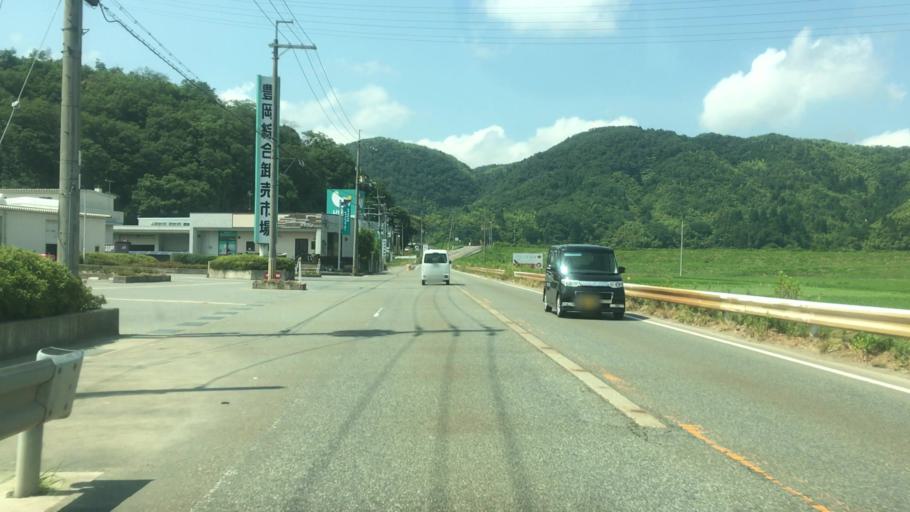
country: JP
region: Hyogo
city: Toyooka
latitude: 35.5605
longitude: 134.7961
